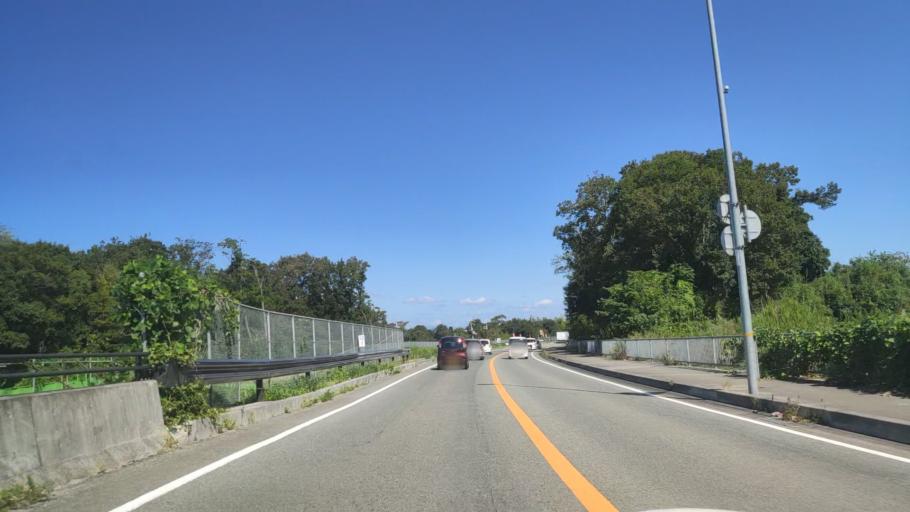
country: JP
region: Hyogo
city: Miki
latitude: 34.7579
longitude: 134.9760
